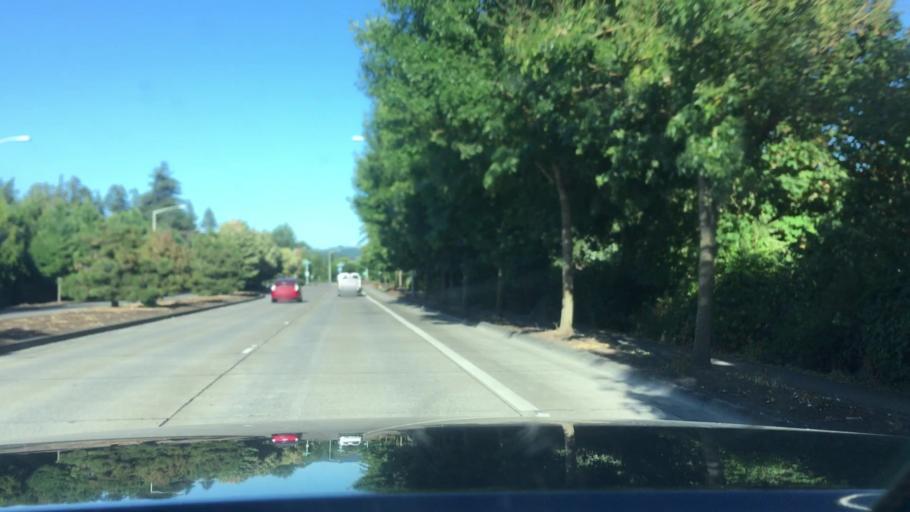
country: US
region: Oregon
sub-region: Lane County
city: Springfield
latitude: 44.0840
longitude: -123.0360
